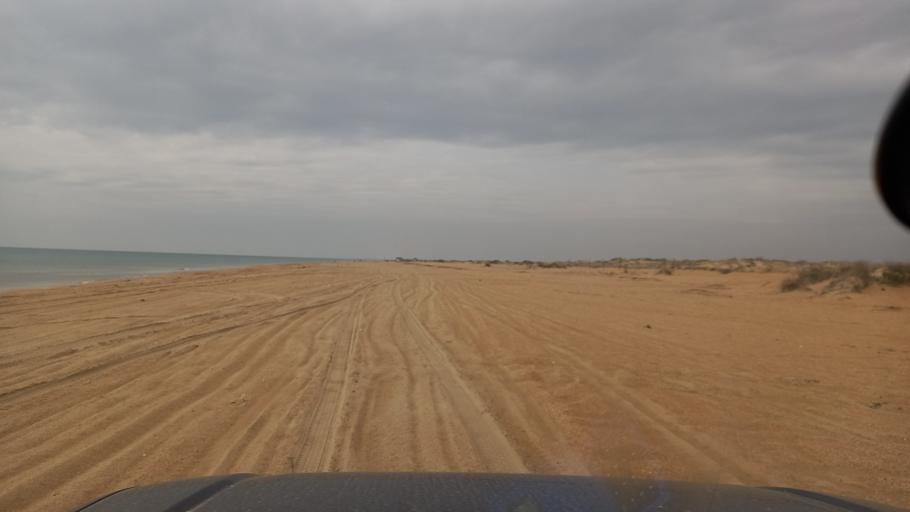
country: RU
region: Krasnodarskiy
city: Vityazevo
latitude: 44.9916
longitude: 37.2319
